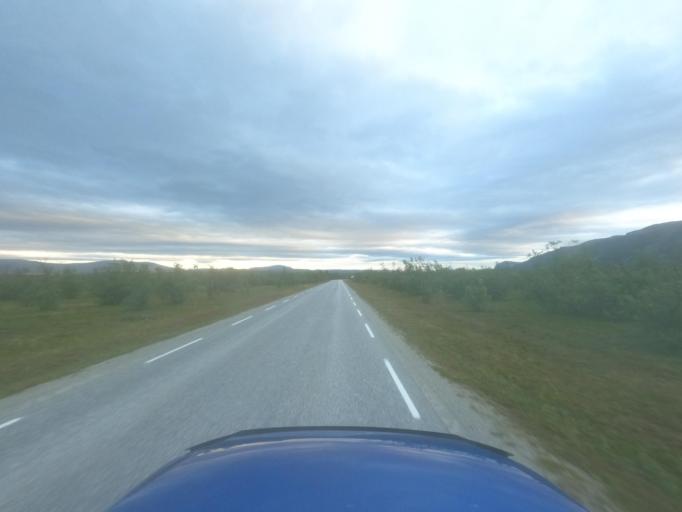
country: NO
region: Finnmark Fylke
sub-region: Porsanger
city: Lakselv
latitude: 70.0705
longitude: 24.9261
